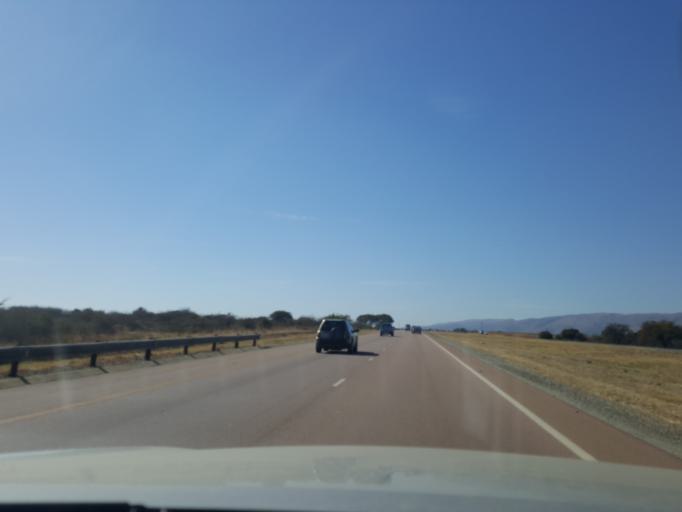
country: ZA
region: North-West
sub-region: Bojanala Platinum District Municipality
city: Brits
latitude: -25.7369
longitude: 27.6129
